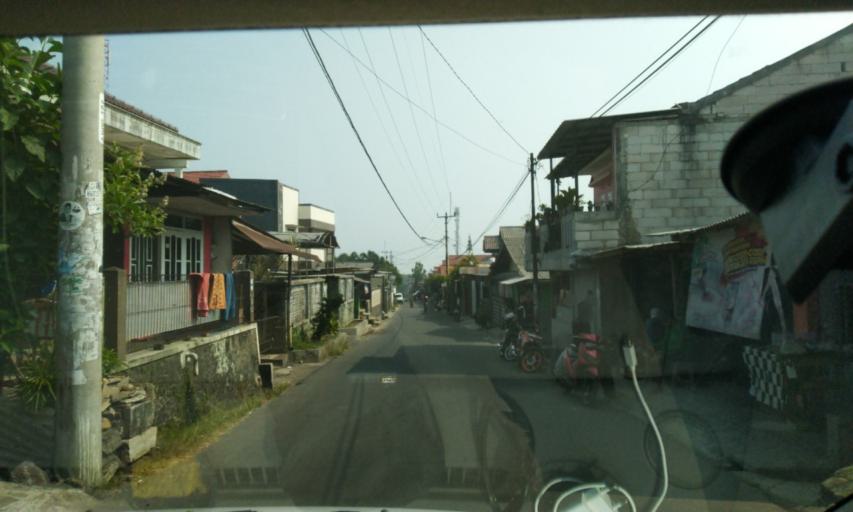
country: ID
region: West Java
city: Caringin
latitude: -6.6690
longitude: 106.8672
